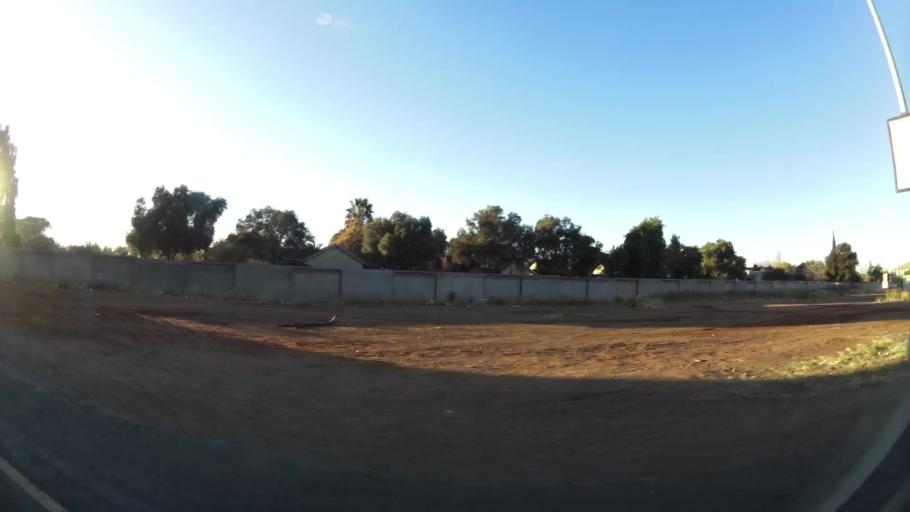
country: ZA
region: Northern Cape
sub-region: Frances Baard District Municipality
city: Kimberley
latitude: -28.7594
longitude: 24.7614
